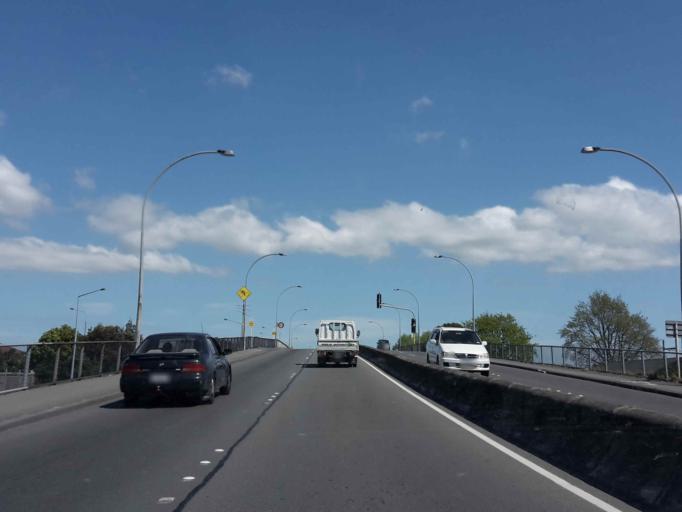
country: NZ
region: Canterbury
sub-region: Selwyn District
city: Prebbleton
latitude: -43.5402
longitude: 172.5515
